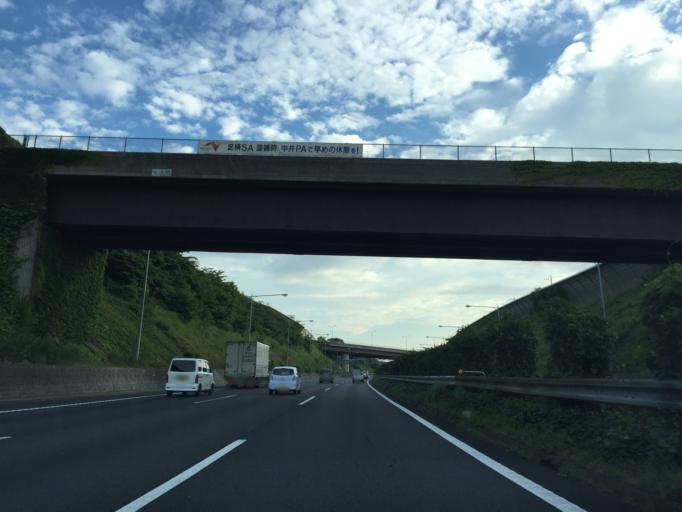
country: JP
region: Kanagawa
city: Hadano
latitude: 35.3656
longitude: 139.2584
